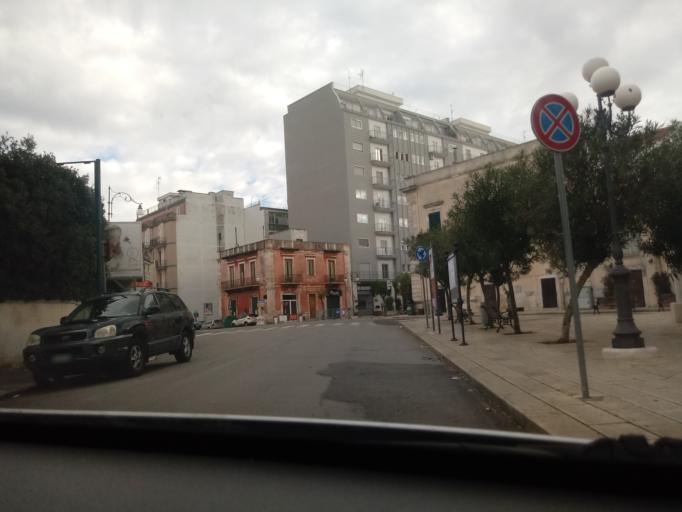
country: IT
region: Apulia
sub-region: Provincia di Bari
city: Putignano
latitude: 40.8526
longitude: 17.1194
